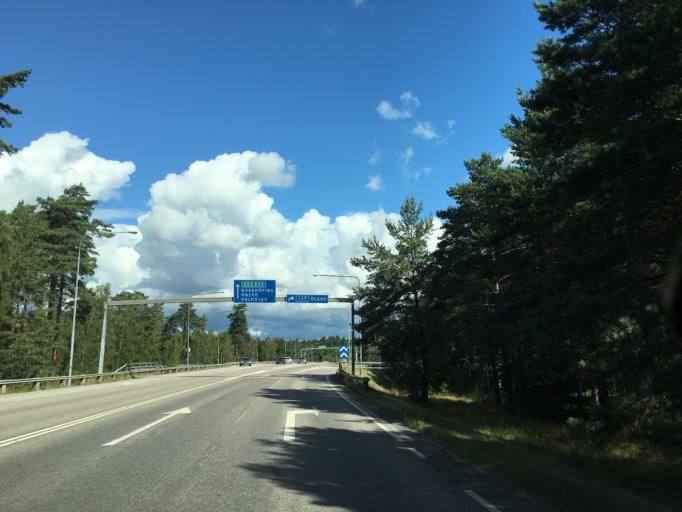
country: SE
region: Kalmar
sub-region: Kalmar Kommun
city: Kalmar
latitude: 56.6830
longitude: 16.3563
